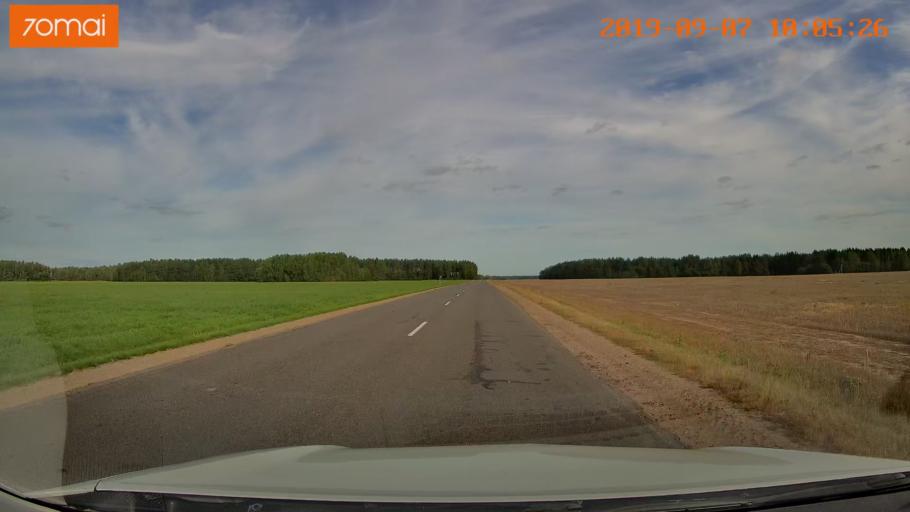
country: BY
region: Grodnenskaya
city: Voranava
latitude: 54.0474
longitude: 25.4074
